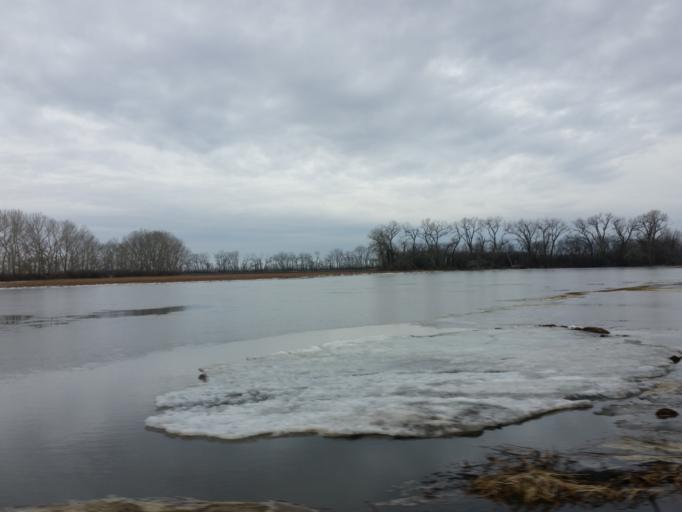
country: US
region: North Dakota
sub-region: Walsh County
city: Grafton
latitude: 48.4025
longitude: -97.4703
